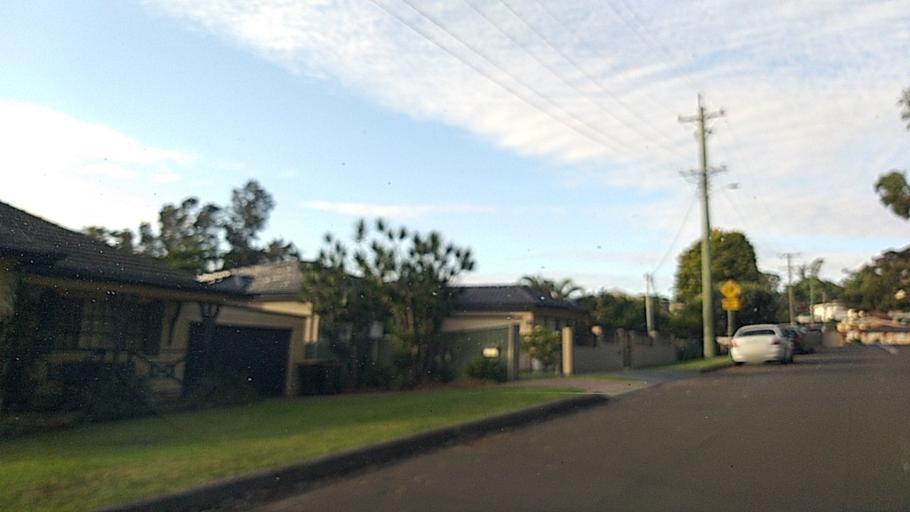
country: AU
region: New South Wales
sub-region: Wollongong
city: Mount Ousley
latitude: -34.3865
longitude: 150.8728
